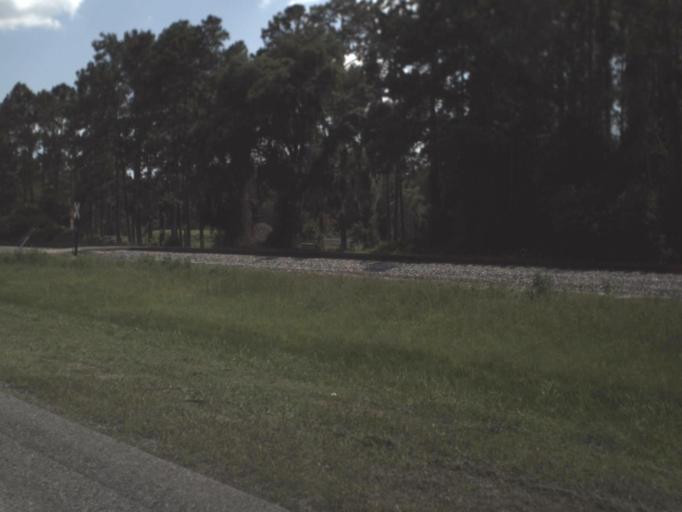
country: US
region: Florida
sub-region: Alachua County
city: Hawthorne
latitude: 29.5419
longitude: -82.1002
